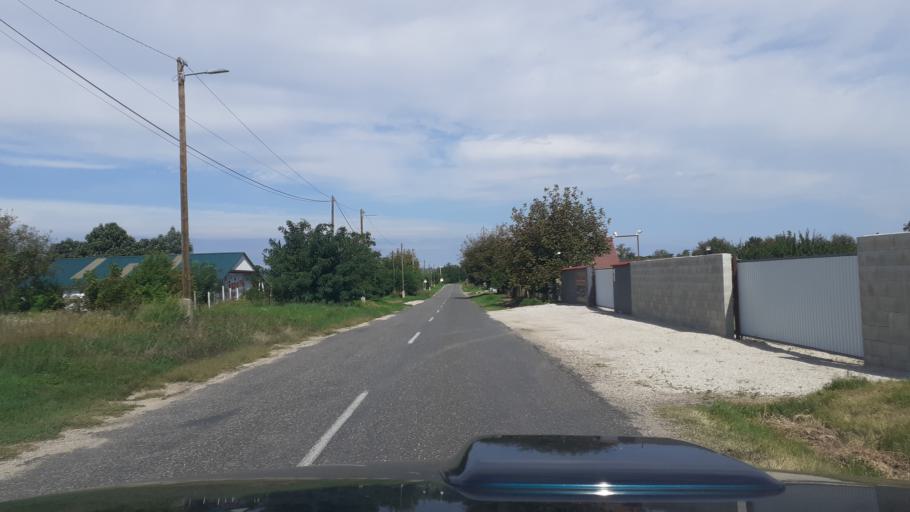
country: HU
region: Fejer
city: Seregelyes
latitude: 47.1220
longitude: 18.5786
